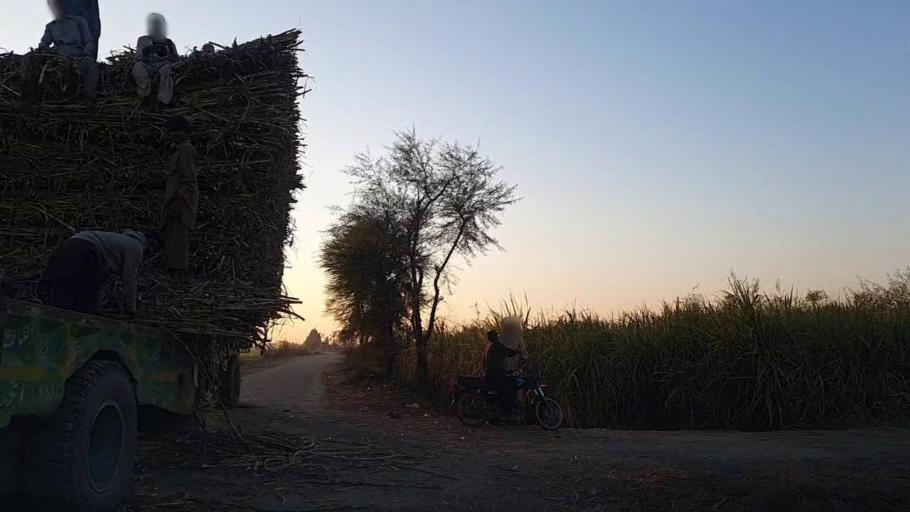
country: PK
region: Sindh
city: Bandhi
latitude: 26.6202
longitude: 68.3588
